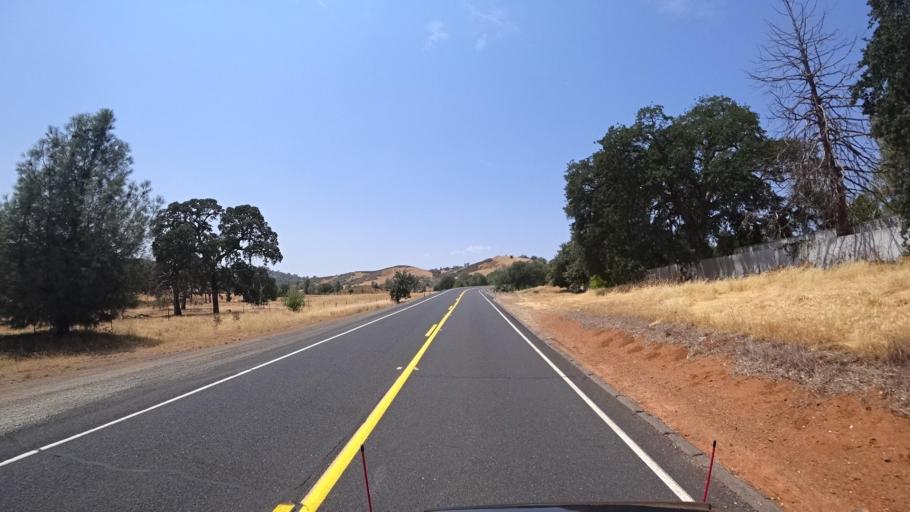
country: US
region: California
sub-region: Tuolumne County
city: Tuolumne City
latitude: 37.7001
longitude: -120.2700
